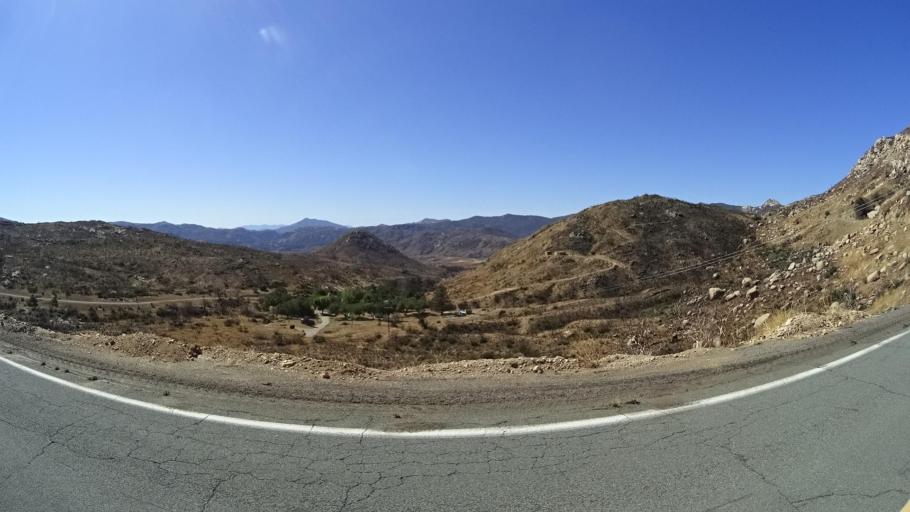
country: US
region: California
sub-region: San Diego County
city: Descanso
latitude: 32.7466
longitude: -116.6733
